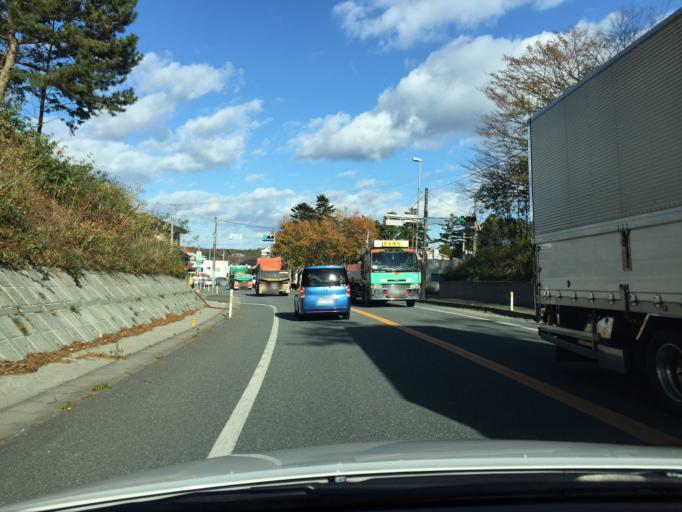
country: JP
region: Fukushima
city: Namie
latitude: 37.3327
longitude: 141.0176
